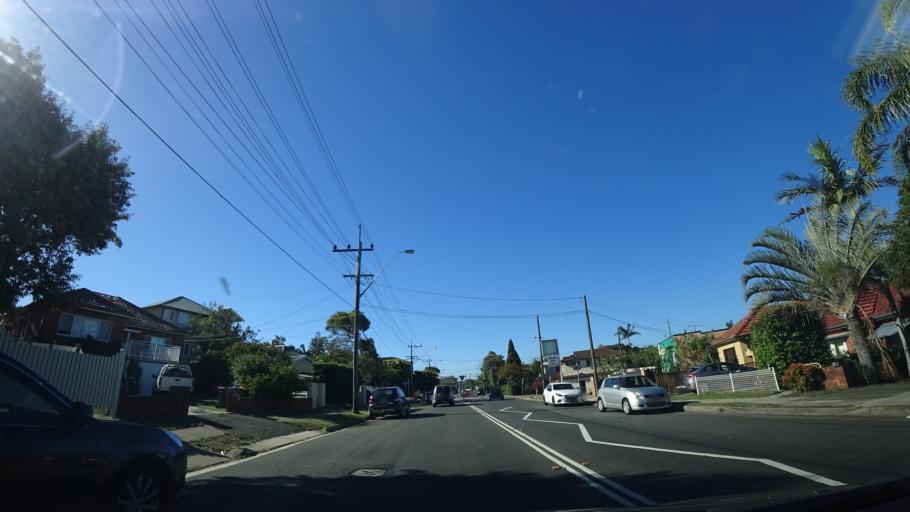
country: AU
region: New South Wales
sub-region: Warringah
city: Freshwater
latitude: -33.7769
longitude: 151.2797
